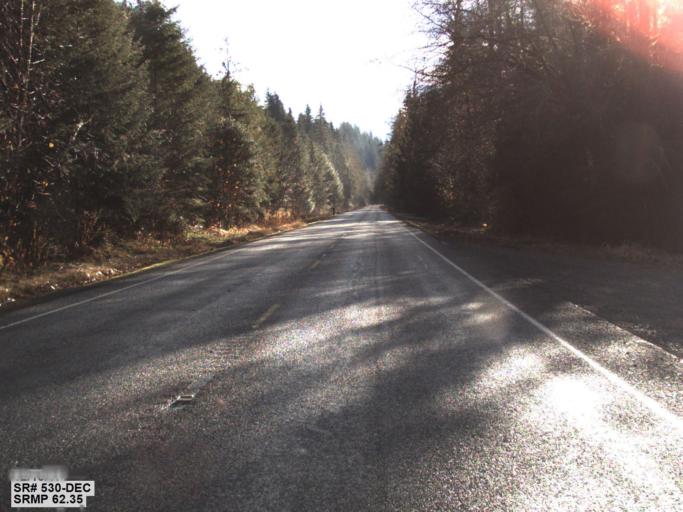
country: US
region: Washington
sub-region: Snohomish County
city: Darrington
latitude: 48.4206
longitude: -121.5614
